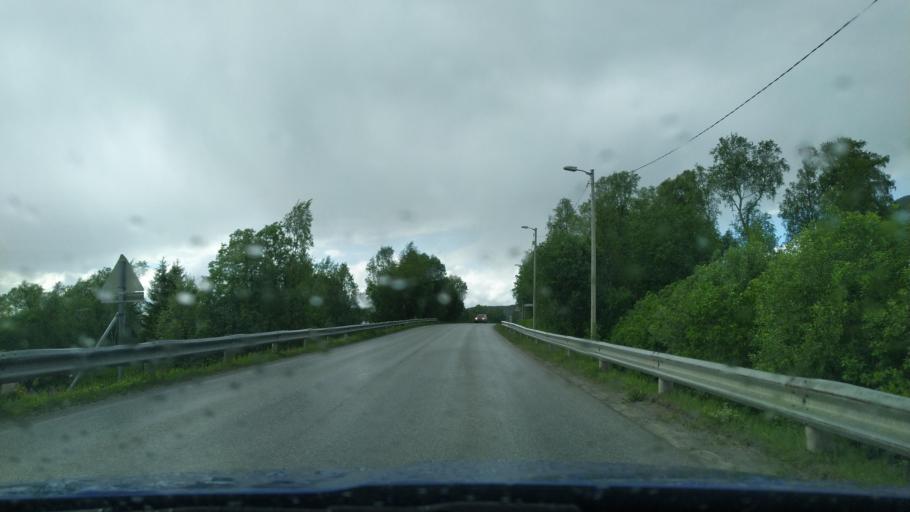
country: NO
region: Troms
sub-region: Sorreisa
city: Sorreisa
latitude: 69.1524
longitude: 18.1669
